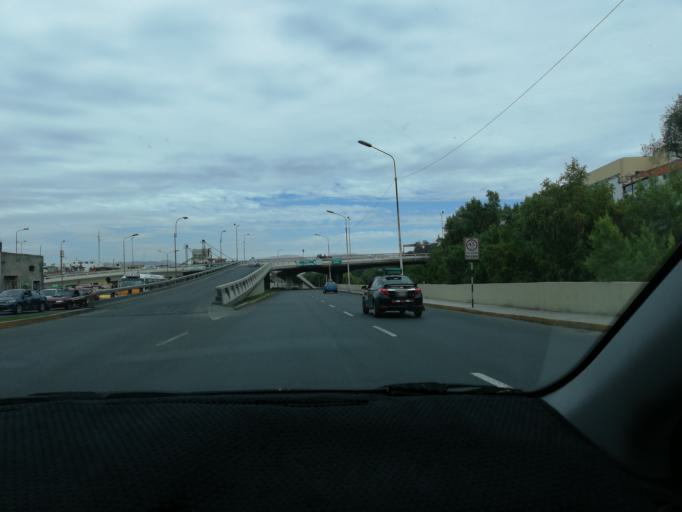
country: PE
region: Arequipa
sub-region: Provincia de Arequipa
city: Arequipa
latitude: -16.3985
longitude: -71.5420
